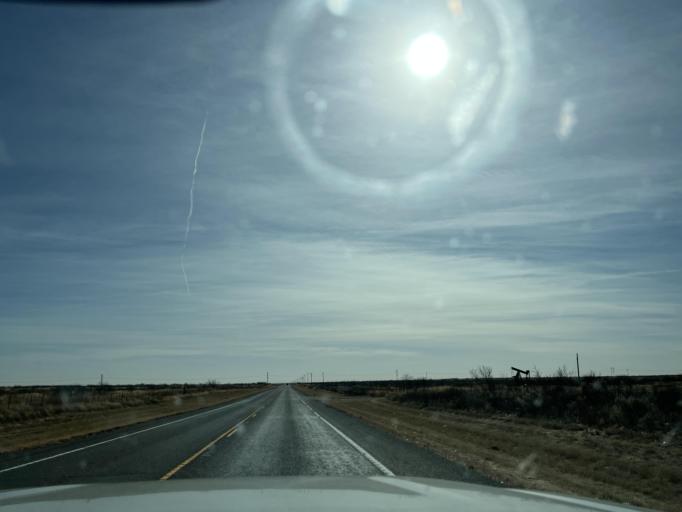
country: US
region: Texas
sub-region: Andrews County
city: Andrews
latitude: 32.4269
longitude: -102.4361
